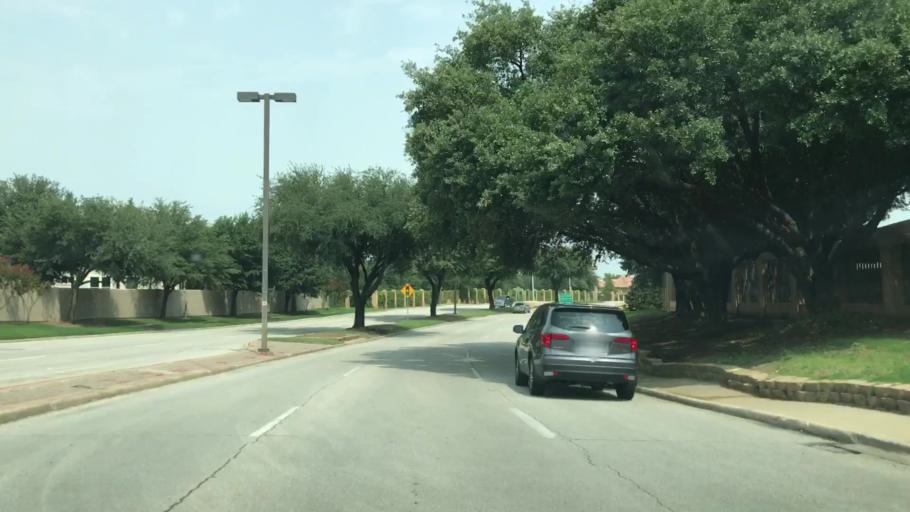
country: US
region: Texas
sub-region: Dallas County
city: Irving
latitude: 32.8615
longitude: -96.9598
